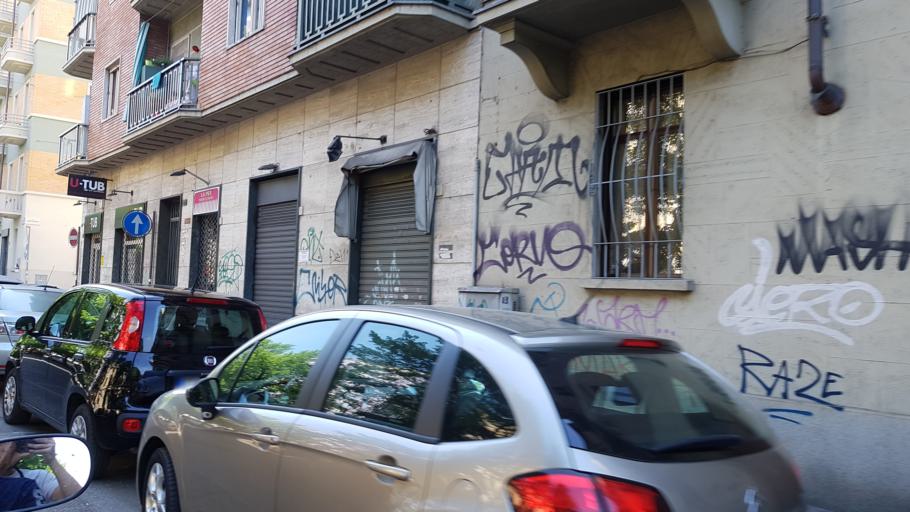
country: IT
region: Piedmont
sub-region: Provincia di Torino
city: Lesna
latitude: 45.0627
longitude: 7.6449
